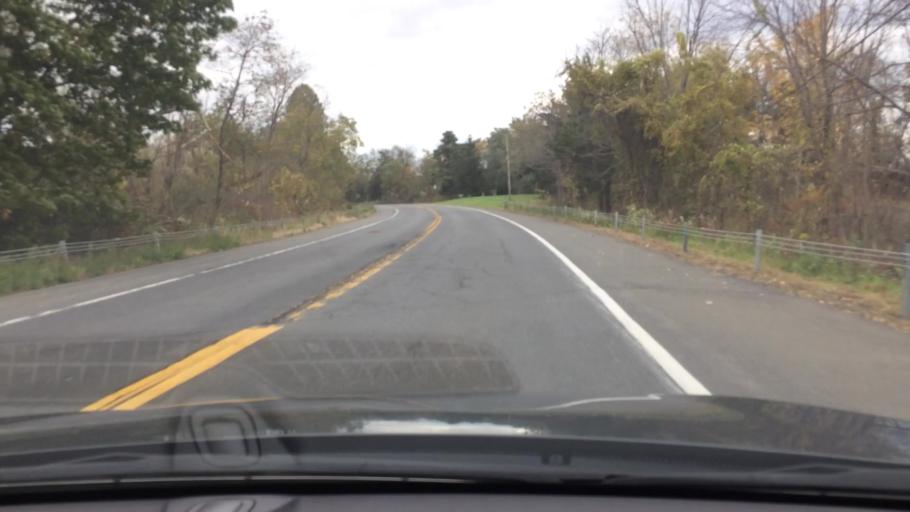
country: US
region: New York
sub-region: Columbia County
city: Oakdale
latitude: 42.1736
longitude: -73.7585
